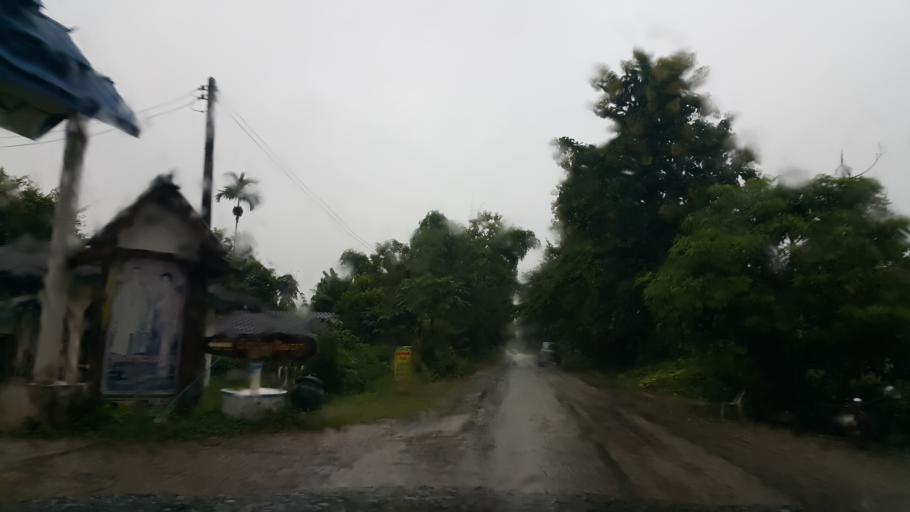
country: TH
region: Phayao
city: Phu Sang
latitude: 19.5929
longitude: 100.3848
